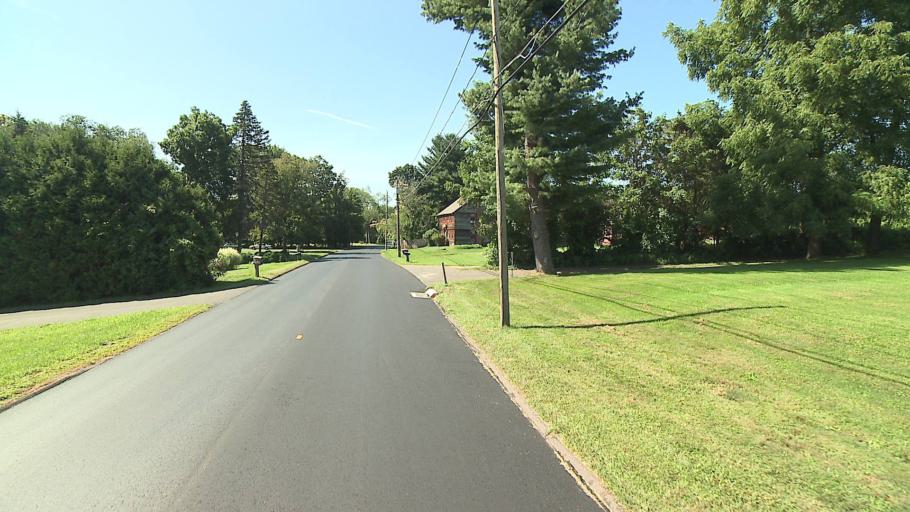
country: US
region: Connecticut
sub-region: Hartford County
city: Tariffville
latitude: 41.9609
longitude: -72.7215
